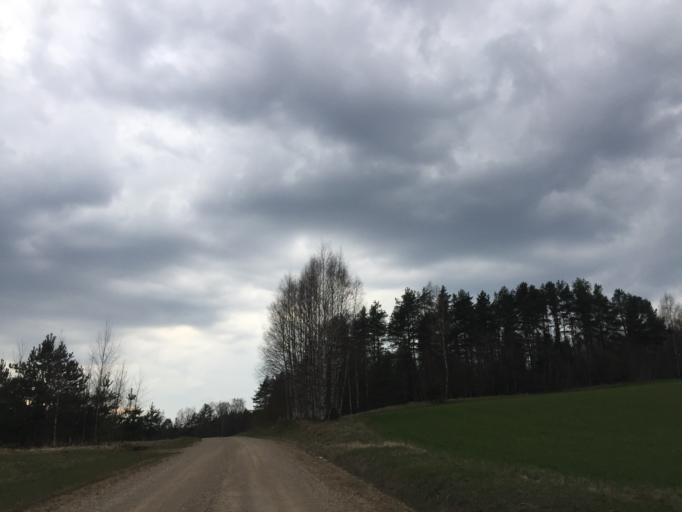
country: EE
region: Vorumaa
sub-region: Antsla vald
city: Vana-Antsla
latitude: 57.9320
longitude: 26.7427
